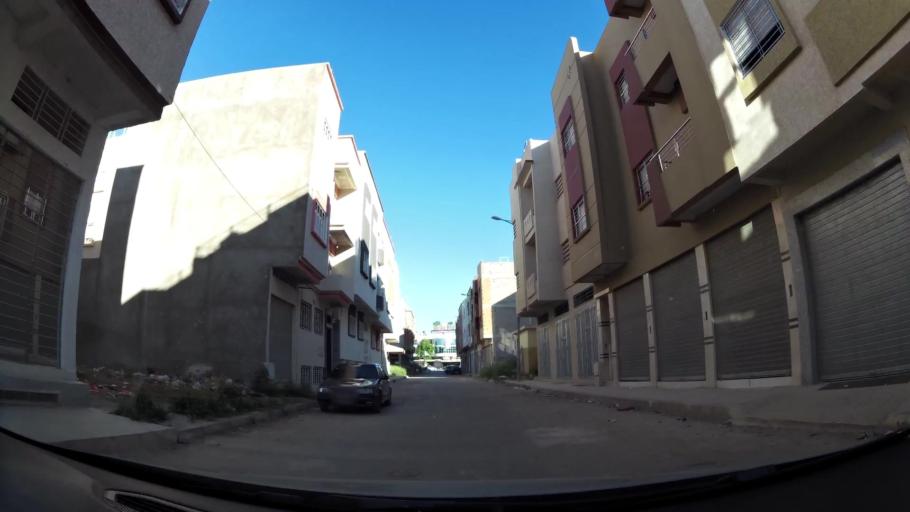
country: MA
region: Fes-Boulemane
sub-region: Fes
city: Fes
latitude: 34.0083
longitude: -5.0110
